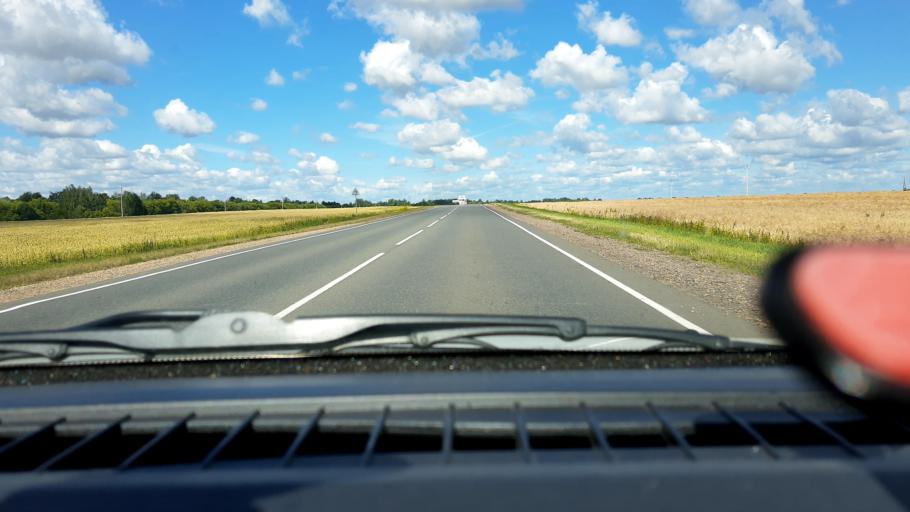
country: RU
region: Nizjnij Novgorod
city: Shatki
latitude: 55.2472
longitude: 44.0020
